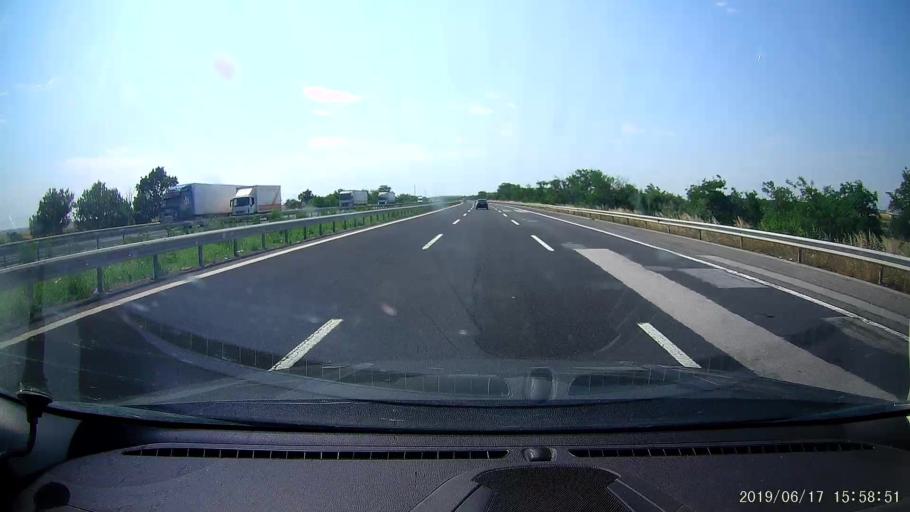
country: TR
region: Tekirdag
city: Velimese
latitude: 41.2218
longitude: 27.9148
